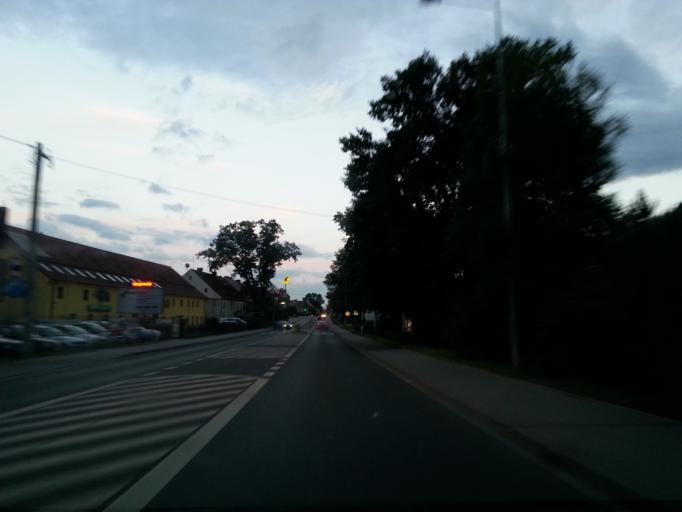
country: PL
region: Lower Silesian Voivodeship
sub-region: Powiat wroclawski
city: Bielany Wroclawskie
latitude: 51.0428
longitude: 16.9696
